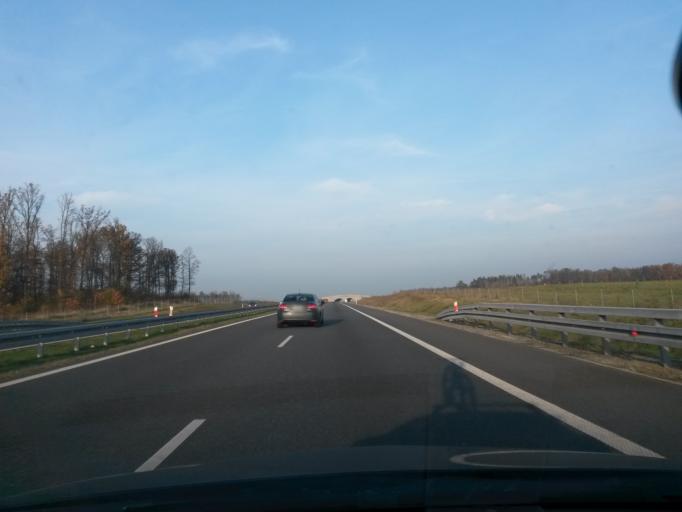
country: PL
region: Lower Silesian Voivodeship
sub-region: Powiat olesnicki
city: Twardogora
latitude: 51.2675
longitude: 17.5517
